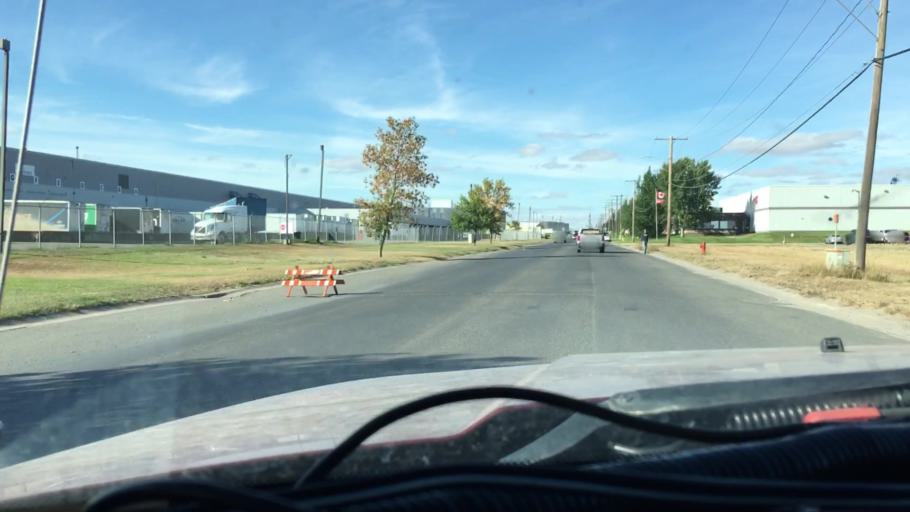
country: CA
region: Saskatchewan
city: Regina
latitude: 50.4703
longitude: -104.5615
